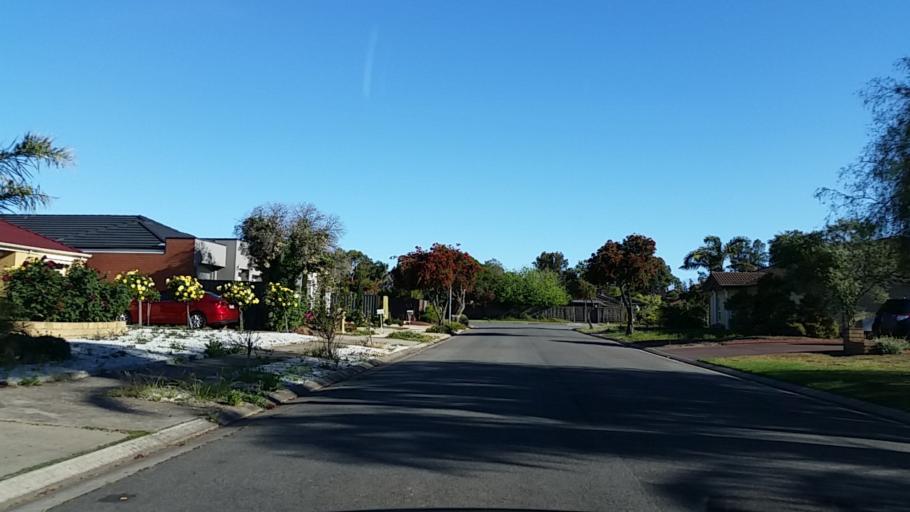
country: AU
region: South Australia
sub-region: Charles Sturt
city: West Lakes Shore
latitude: -34.8673
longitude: 138.4982
